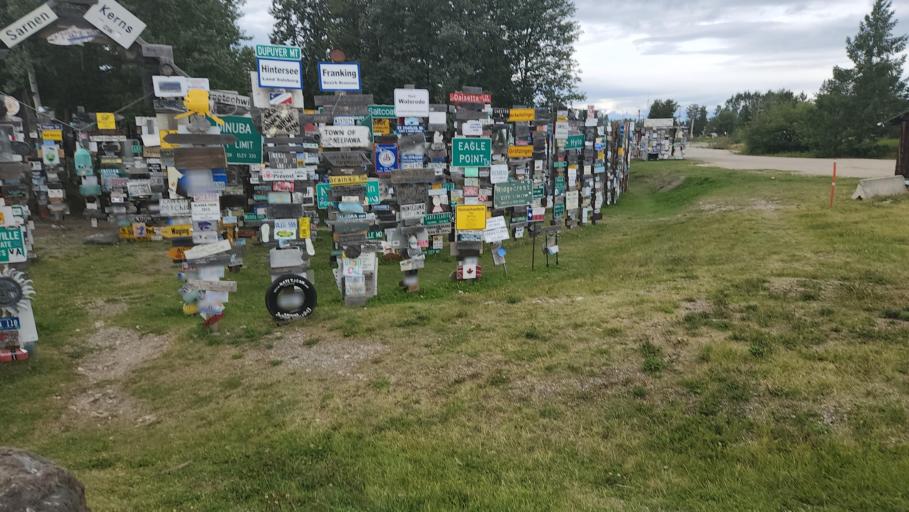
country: CA
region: Yukon
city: Watson Lake
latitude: 60.0634
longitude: -128.7123
